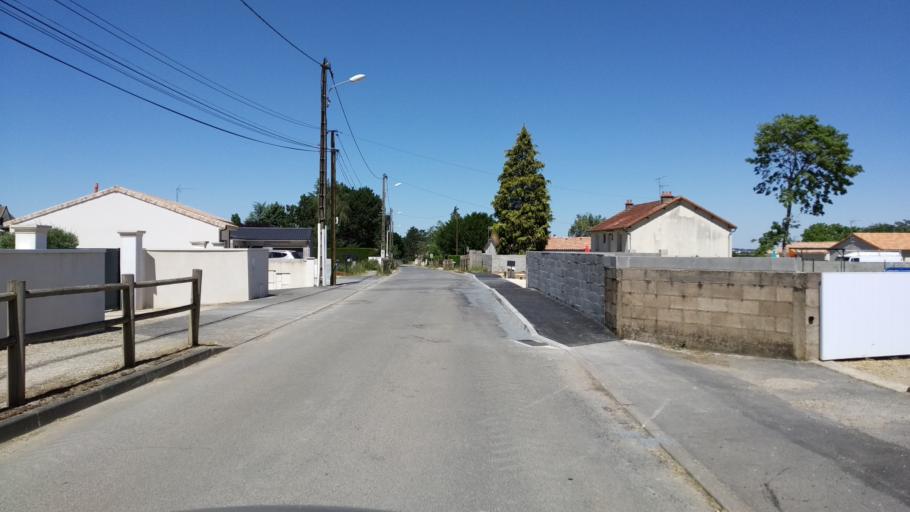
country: FR
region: Poitou-Charentes
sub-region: Departement de la Vienne
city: Vouneuil-sous-Biard
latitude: 46.5967
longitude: 0.2809
